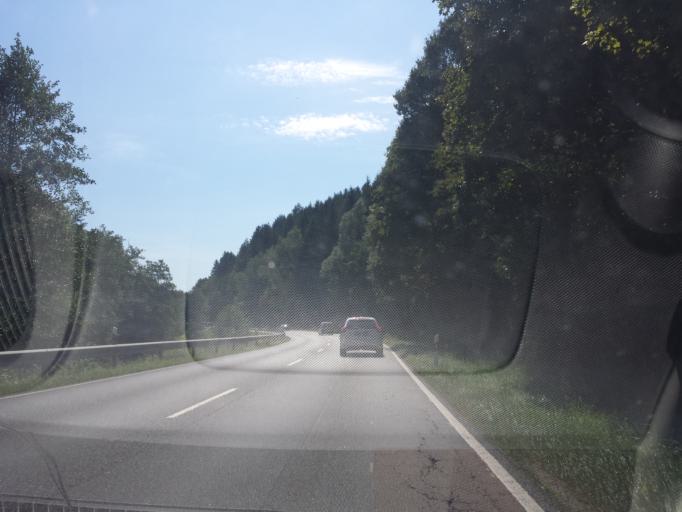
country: DE
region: Bavaria
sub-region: Upper Palatinate
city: Traitsching
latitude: 49.1360
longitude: 12.6522
